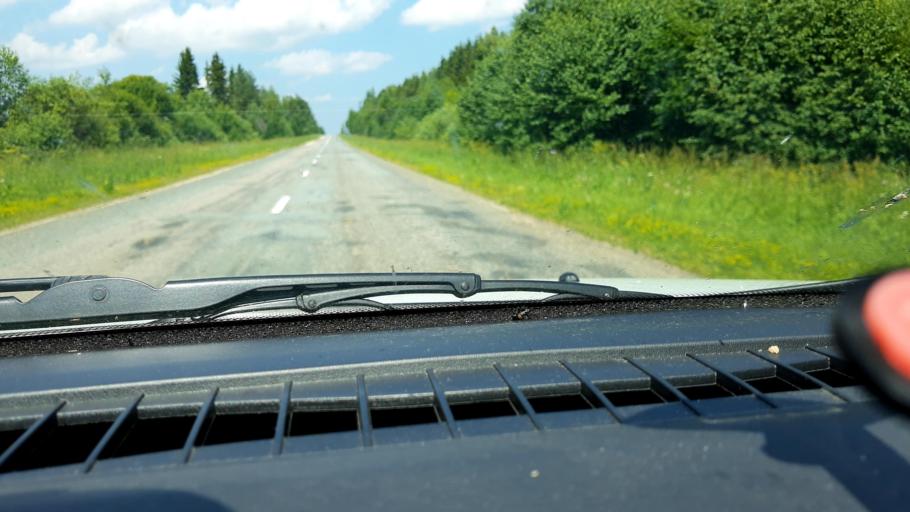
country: RU
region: Nizjnij Novgorod
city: Sharanga
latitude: 57.0935
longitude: 46.5330
